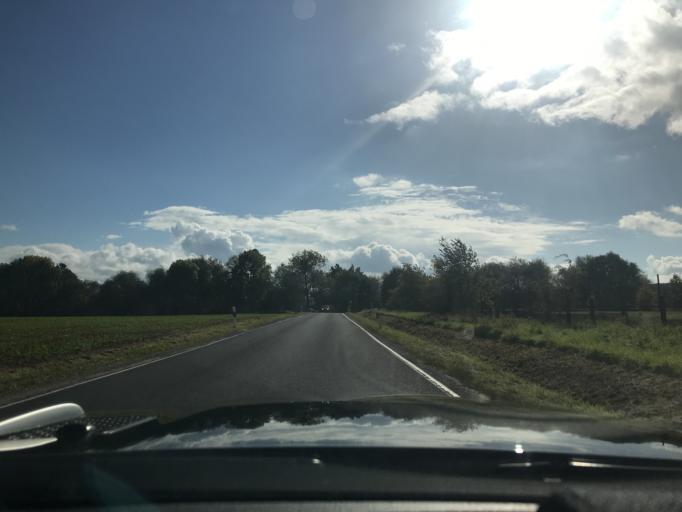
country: DE
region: Thuringia
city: Oberdorla
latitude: 51.1717
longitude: 10.3970
